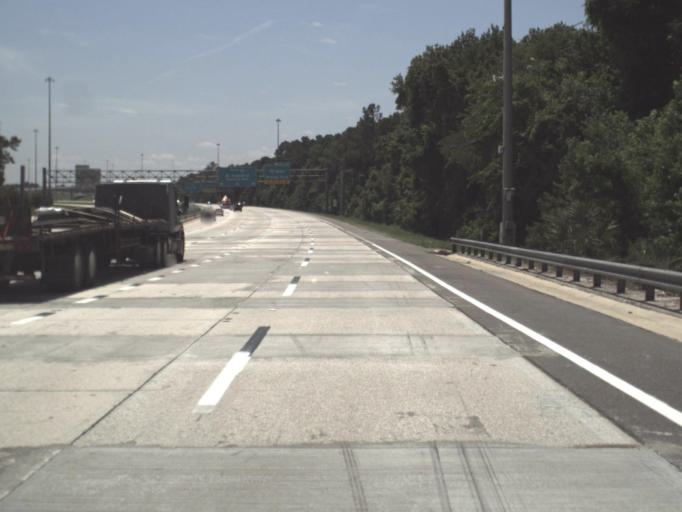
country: US
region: Florida
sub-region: Saint Johns County
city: Fruit Cove
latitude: 30.1801
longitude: -81.5591
